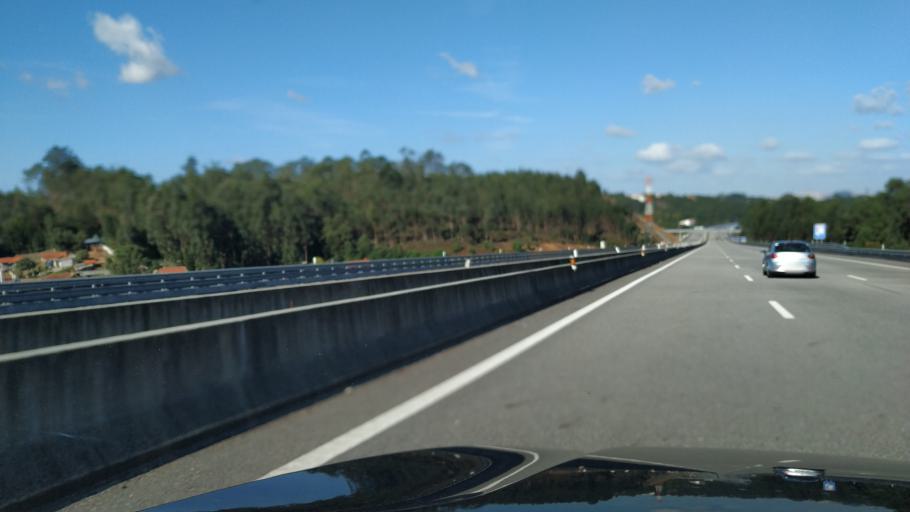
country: PT
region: Porto
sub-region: Vila Nova de Gaia
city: Olival
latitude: 41.0641
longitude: -8.5295
